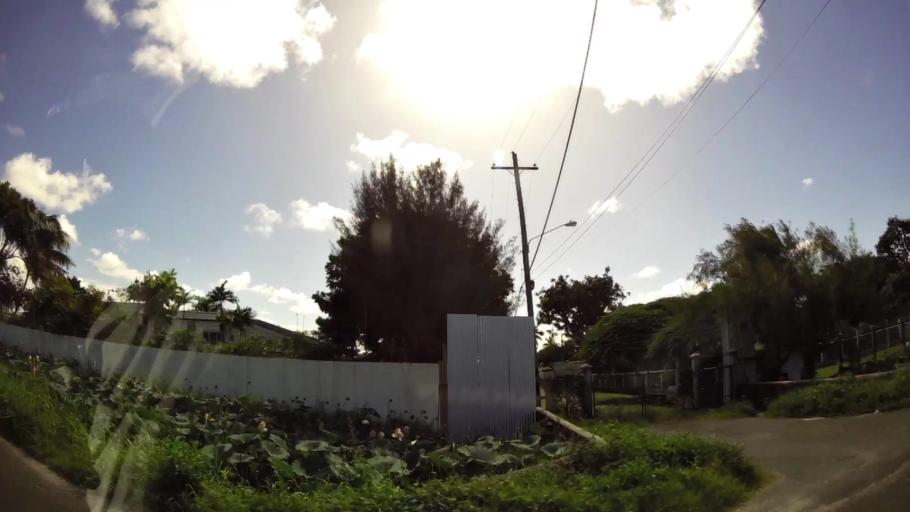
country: GY
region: Demerara-Mahaica
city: Georgetown
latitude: 6.8243
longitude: -58.1298
